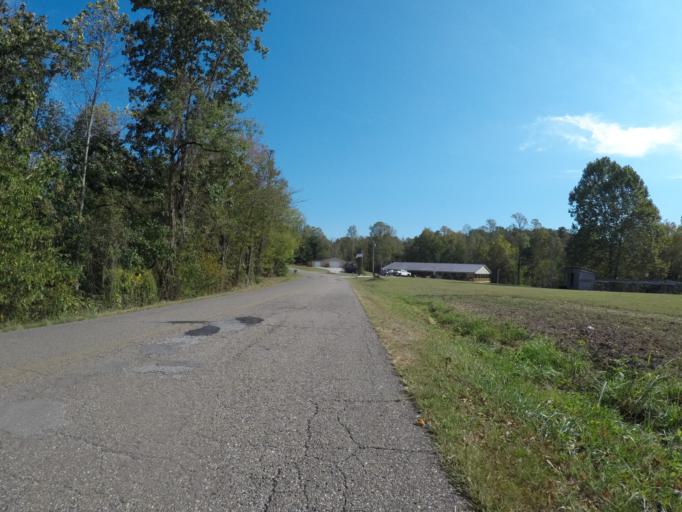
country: US
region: West Virginia
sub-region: Cabell County
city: Lesage
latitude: 38.5966
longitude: -82.4155
